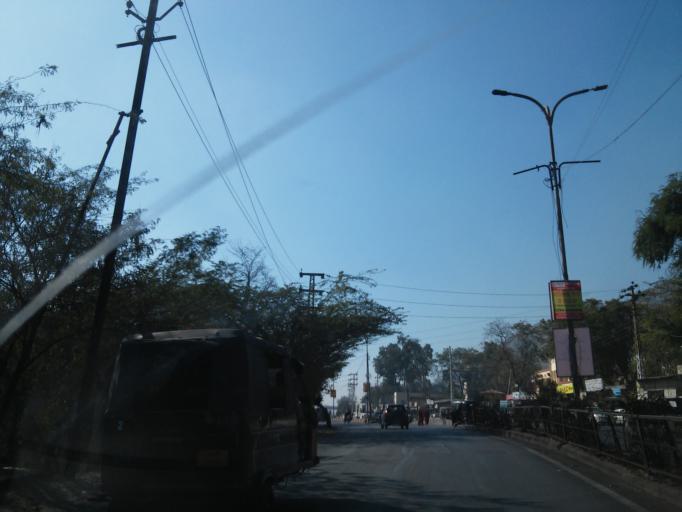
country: IN
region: Rajasthan
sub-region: Udaipur
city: Udaipur
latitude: 24.5646
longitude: 73.6937
